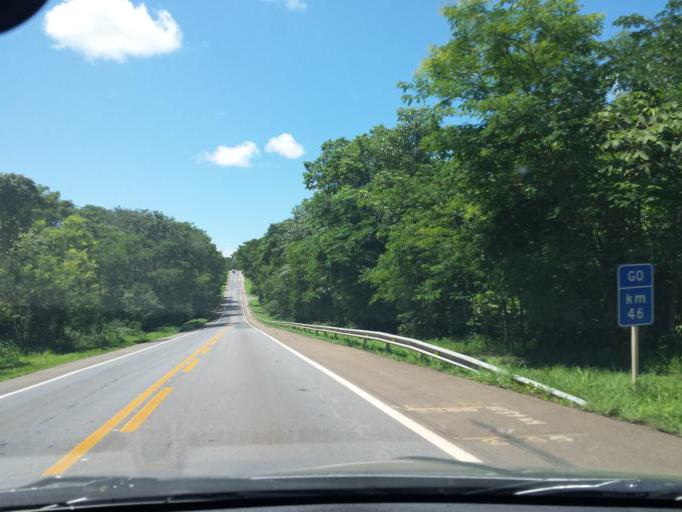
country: BR
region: Goias
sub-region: Luziania
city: Luziania
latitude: -16.4109
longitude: -47.8235
